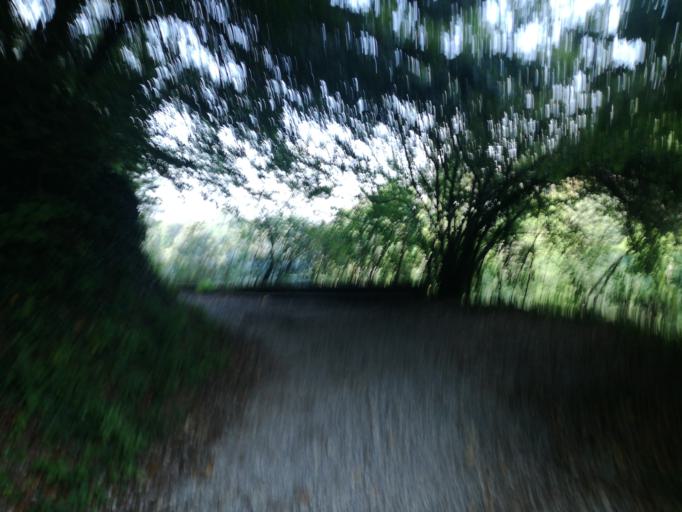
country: IT
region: Lombardy
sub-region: Provincia di Lecco
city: Imbersago
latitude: 45.7116
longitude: 9.4519
